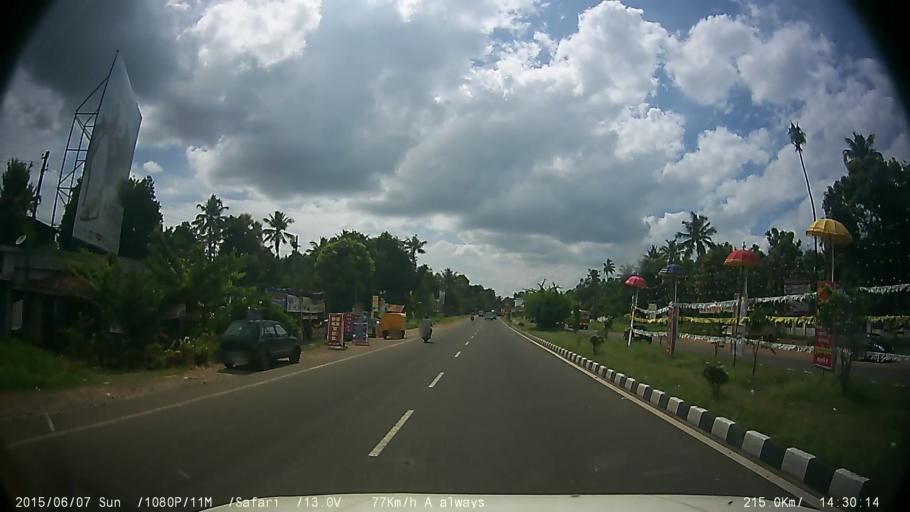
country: IN
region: Kerala
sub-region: Thrissur District
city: Kizhake Chalakudi
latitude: 10.2743
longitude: 76.3463
